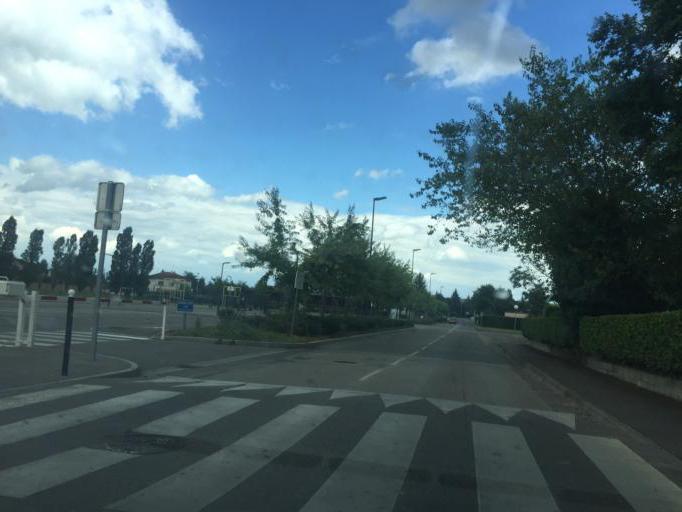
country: FR
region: Rhone-Alpes
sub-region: Departement de l'Isere
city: Pont-de-Cheruy
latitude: 45.7668
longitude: 5.1925
